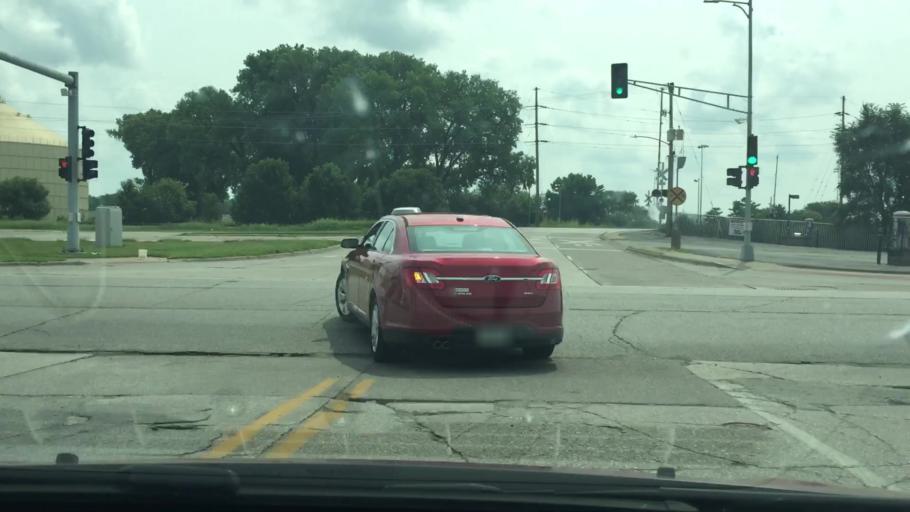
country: US
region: Iowa
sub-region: Muscatine County
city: Muscatine
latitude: 41.4088
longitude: -91.0639
